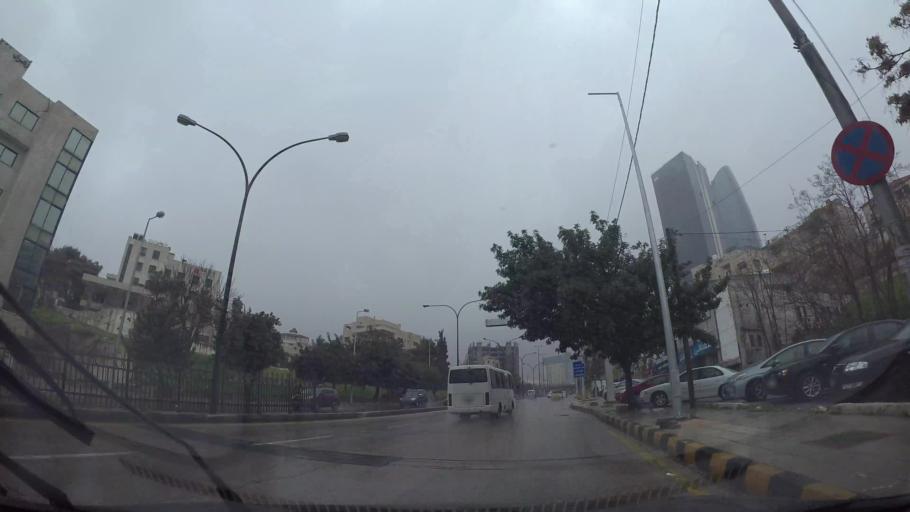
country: JO
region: Amman
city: Amman
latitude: 31.9615
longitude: 35.9039
